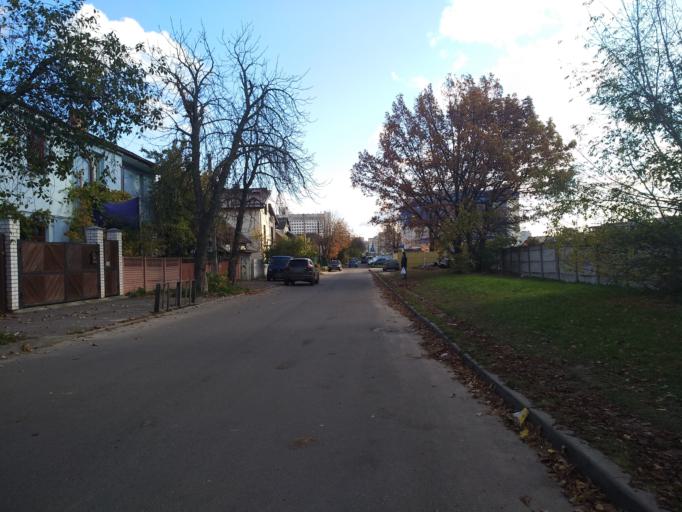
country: BY
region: Minsk
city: Minsk
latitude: 53.9403
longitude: 27.5733
